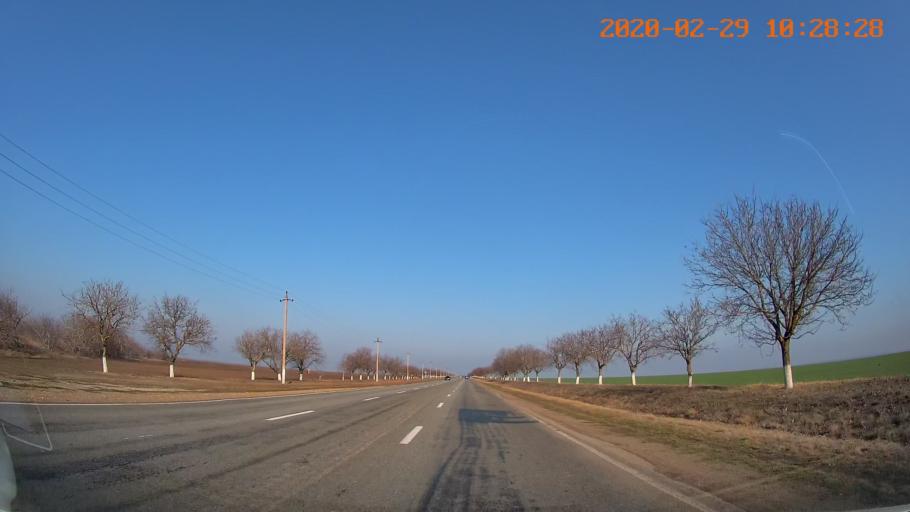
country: MD
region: Telenesti
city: Tiraspolul Nou
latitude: 46.9108
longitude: 29.5913
